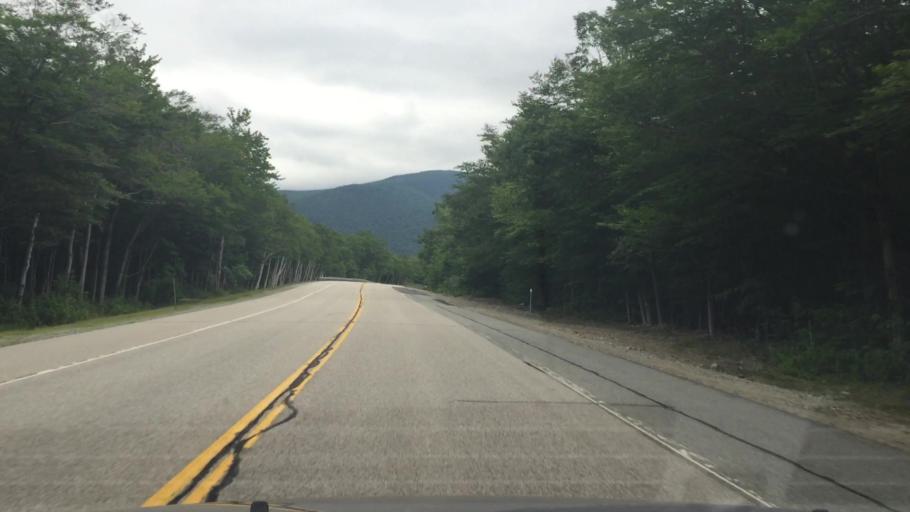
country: US
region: New Hampshire
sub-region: Grafton County
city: Deerfield
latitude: 44.1707
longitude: -71.3870
